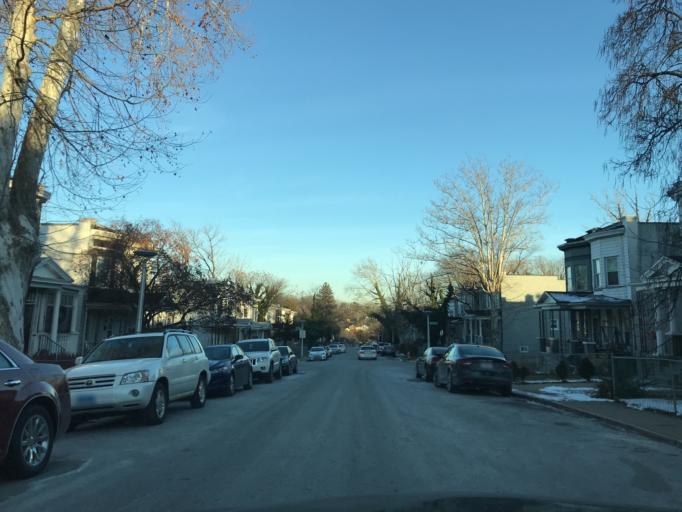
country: US
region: Maryland
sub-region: City of Baltimore
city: Baltimore
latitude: 39.3397
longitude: -76.6057
